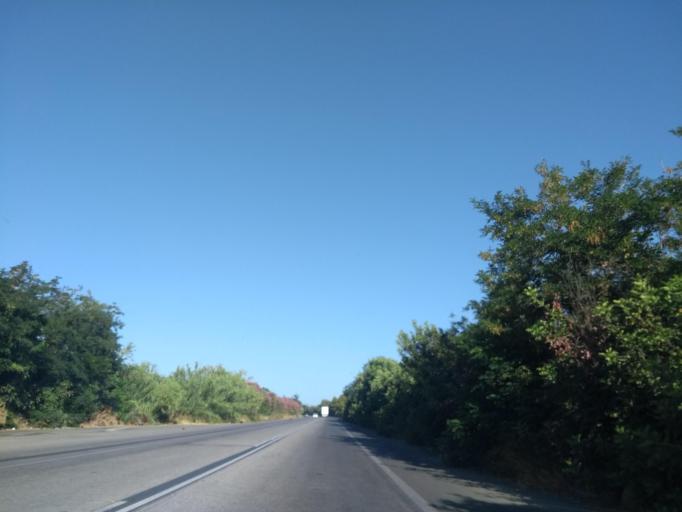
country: GR
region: Crete
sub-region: Nomos Chanias
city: Gerani
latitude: 35.5155
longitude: 23.8673
